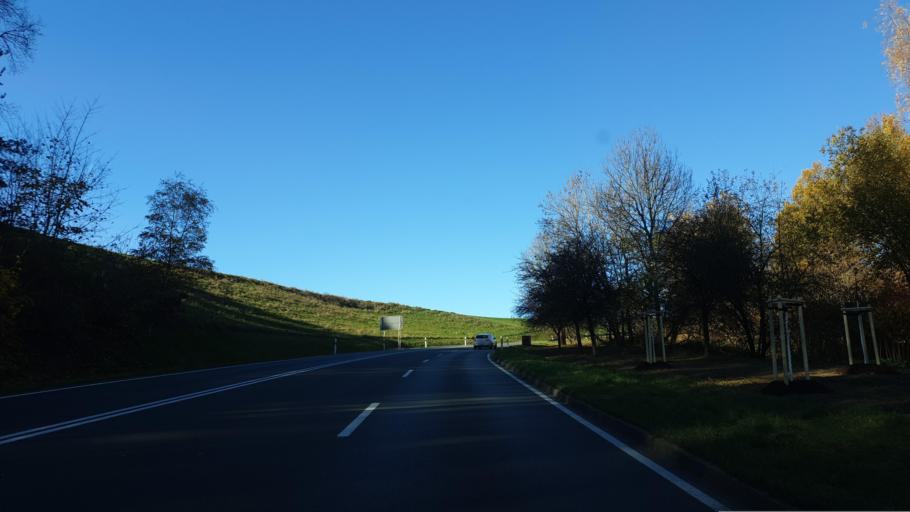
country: DE
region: Thuringia
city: Greiz
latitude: 50.6647
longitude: 12.1570
